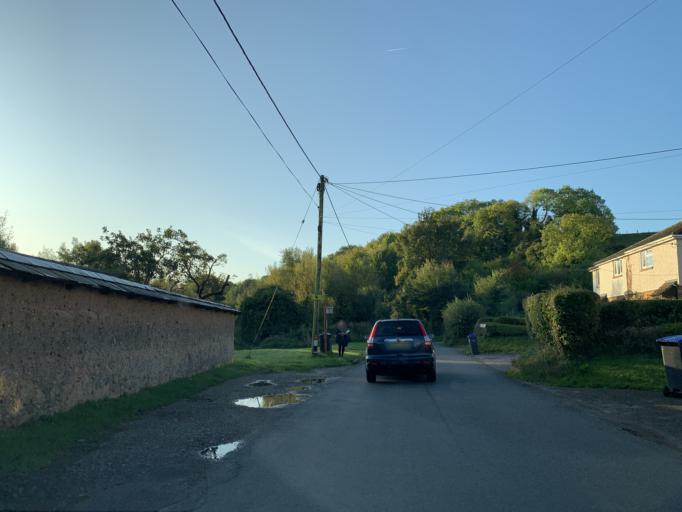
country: GB
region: England
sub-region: Wiltshire
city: Woodford
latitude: 51.1218
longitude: -1.8297
